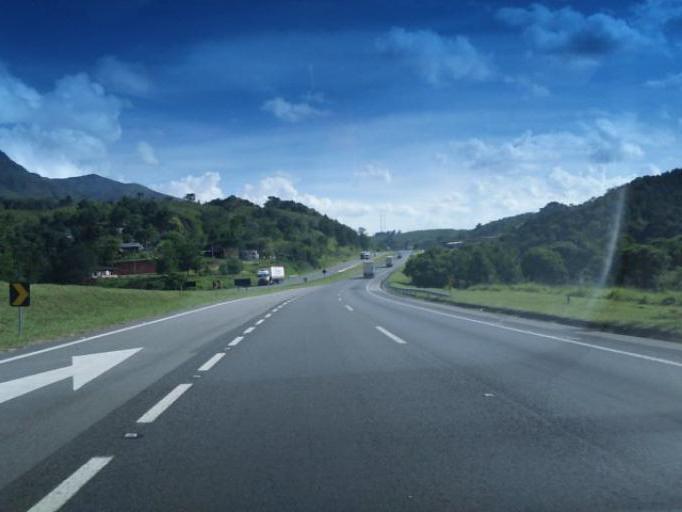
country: BR
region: Parana
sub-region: Campina Grande Do Sul
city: Campina Grande do Sul
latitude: -25.1166
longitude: -48.8540
